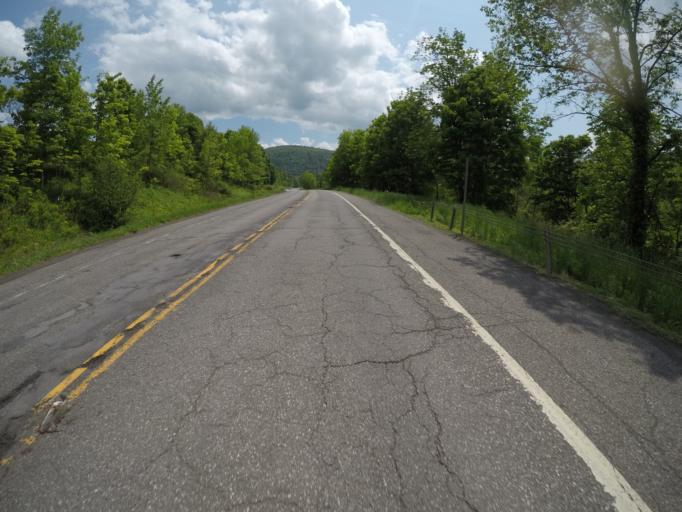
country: US
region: New York
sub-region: Delaware County
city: Stamford
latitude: 42.1922
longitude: -74.5988
